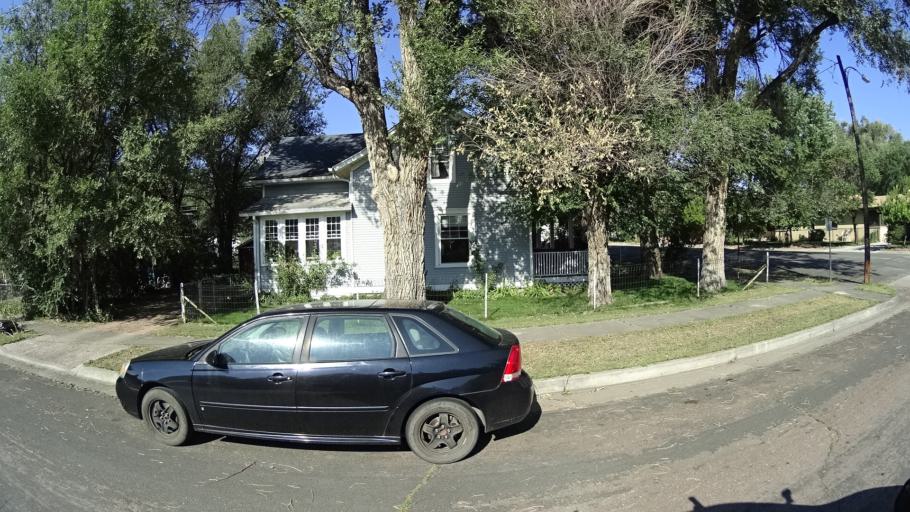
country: US
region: Colorado
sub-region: El Paso County
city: Colorado Springs
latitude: 38.8721
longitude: -104.8256
